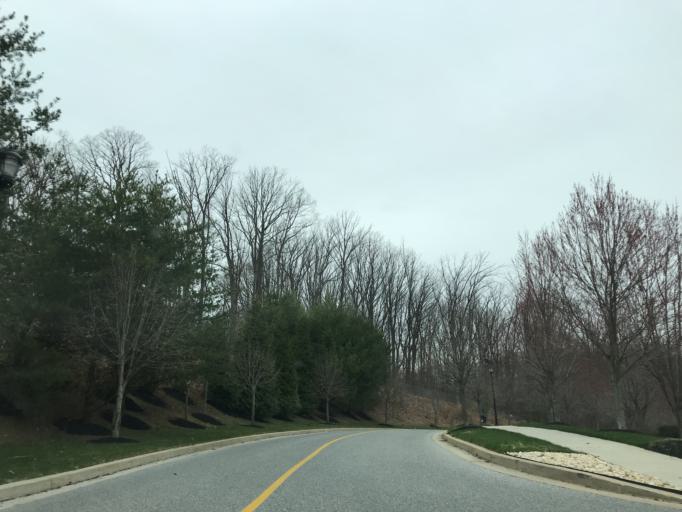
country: US
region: Maryland
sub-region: Baltimore County
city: Pikesville
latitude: 39.3812
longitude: -76.6965
